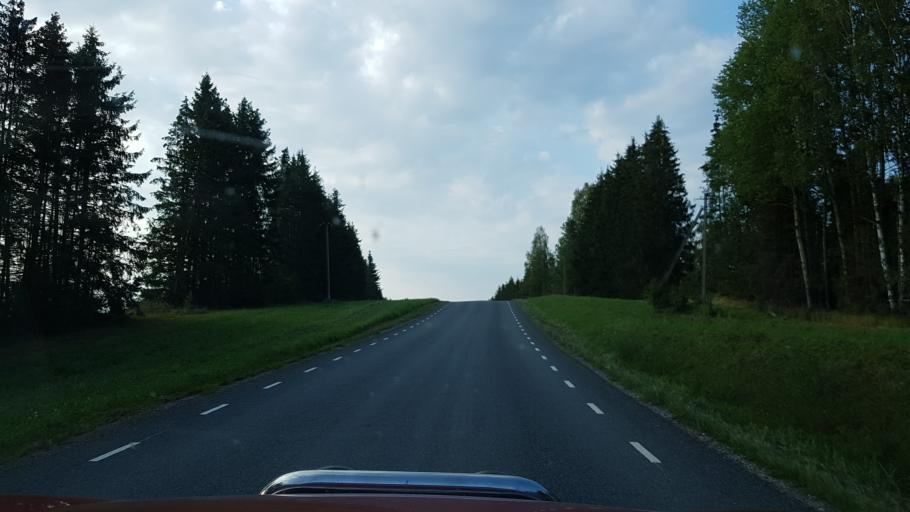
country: EE
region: Tartu
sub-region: UElenurme vald
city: Ulenurme
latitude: 58.1676
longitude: 26.8395
